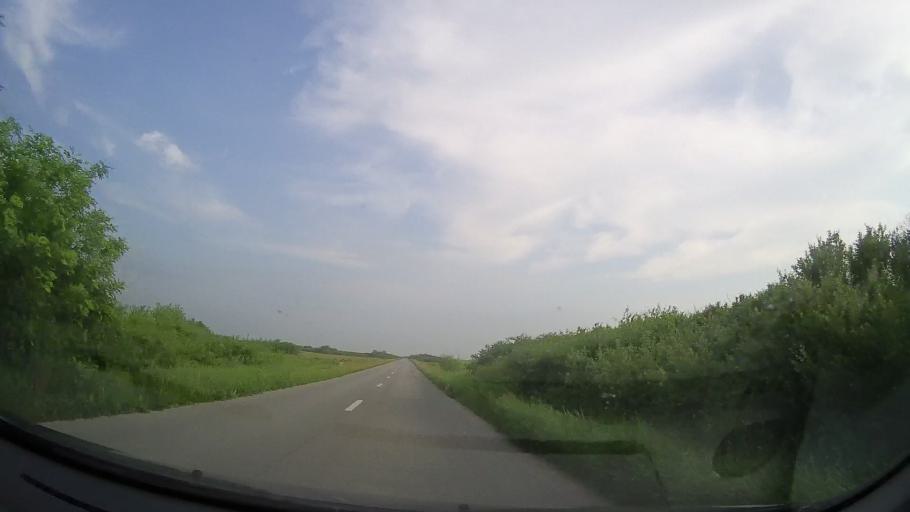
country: RS
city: Jasa Tomic
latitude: 45.4743
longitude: 20.8482
